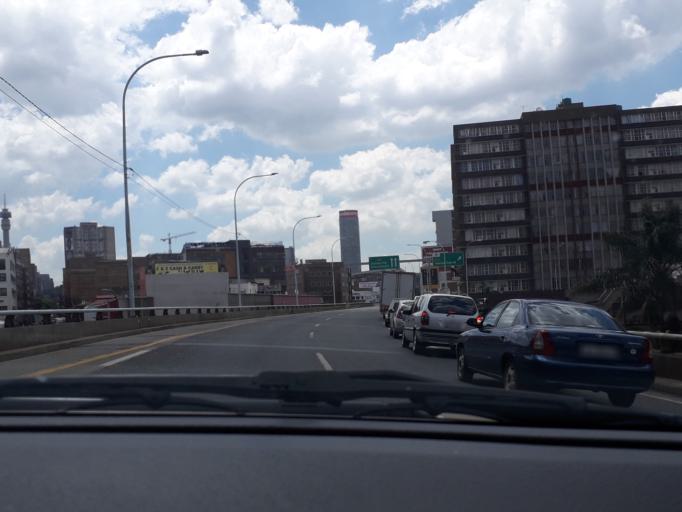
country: ZA
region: Gauteng
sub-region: City of Johannesburg Metropolitan Municipality
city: Johannesburg
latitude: -26.2045
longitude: 28.0544
